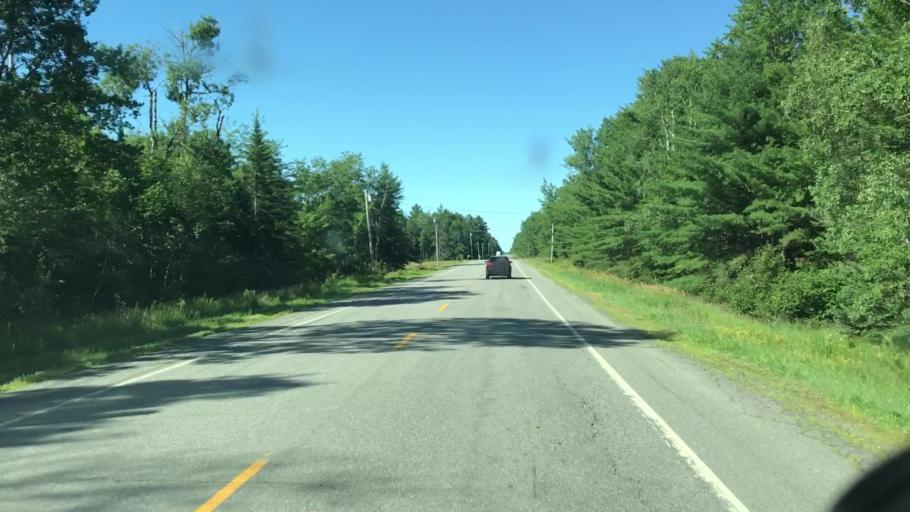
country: US
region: Maine
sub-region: Penobscot County
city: Enfield
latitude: 45.3224
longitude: -68.5973
